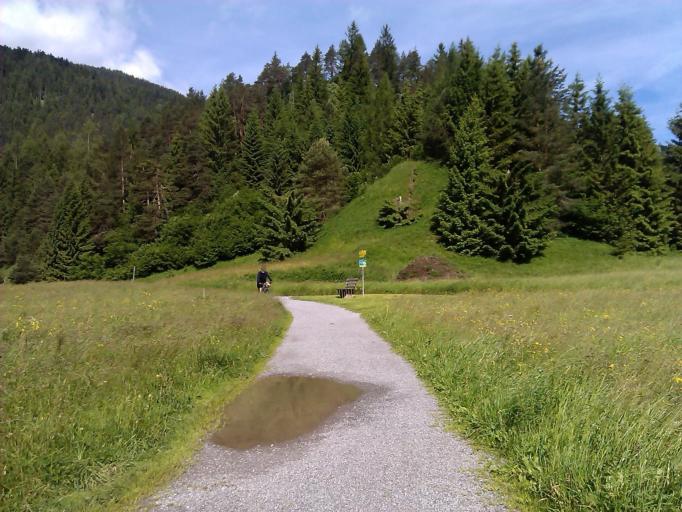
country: AT
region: Tyrol
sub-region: Politischer Bezirk Reutte
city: Biberwier
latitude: 47.3824
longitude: 10.8991
